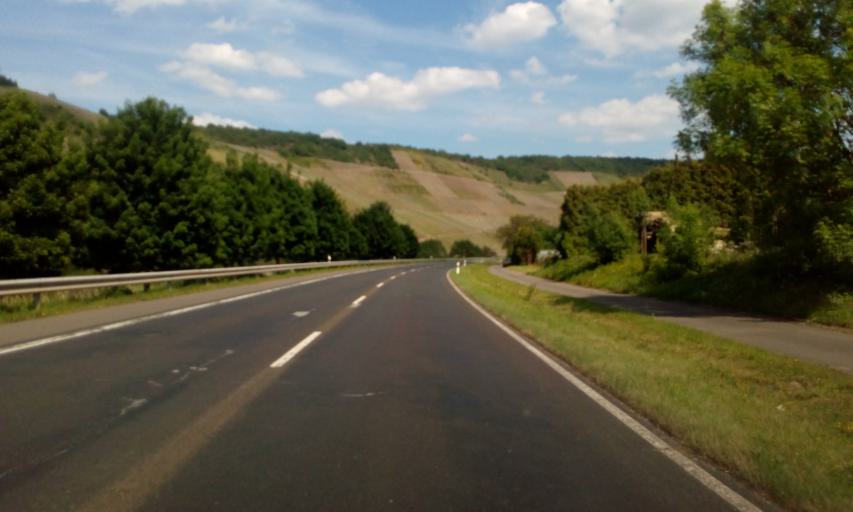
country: DE
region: Rheinland-Pfalz
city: Klusserath
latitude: 49.8428
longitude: 6.8660
